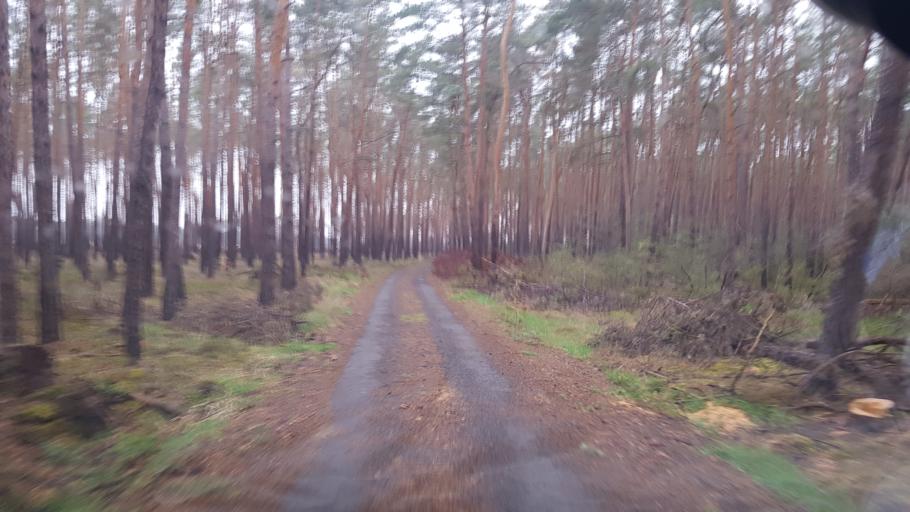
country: DE
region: Brandenburg
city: Bad Liebenwerda
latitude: 51.4964
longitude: 13.2990
